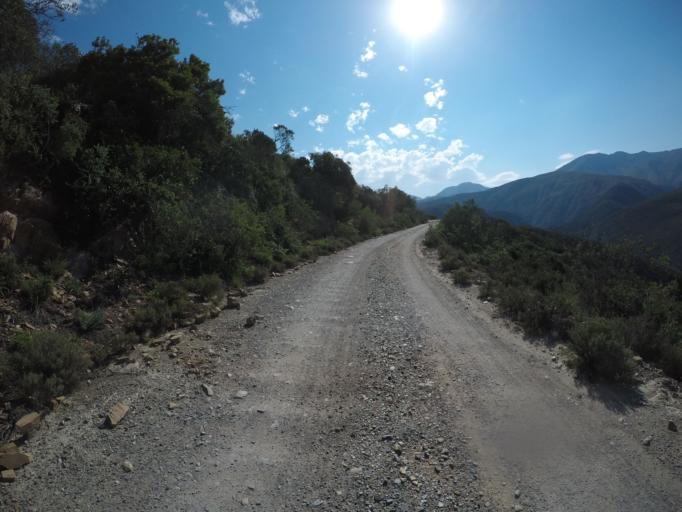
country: ZA
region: Eastern Cape
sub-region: Cacadu District Municipality
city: Kareedouw
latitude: -33.6494
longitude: 24.3508
